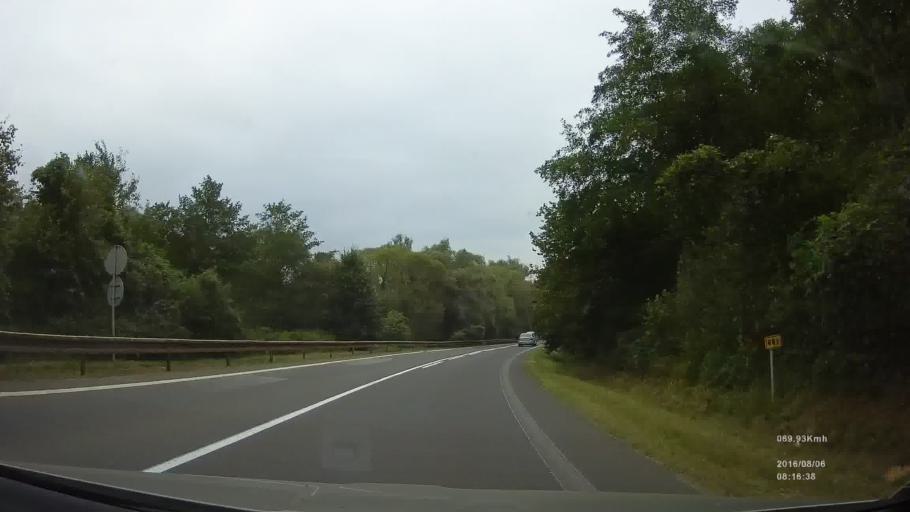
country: SK
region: Presovsky
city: Stropkov
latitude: 49.2130
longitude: 21.6430
